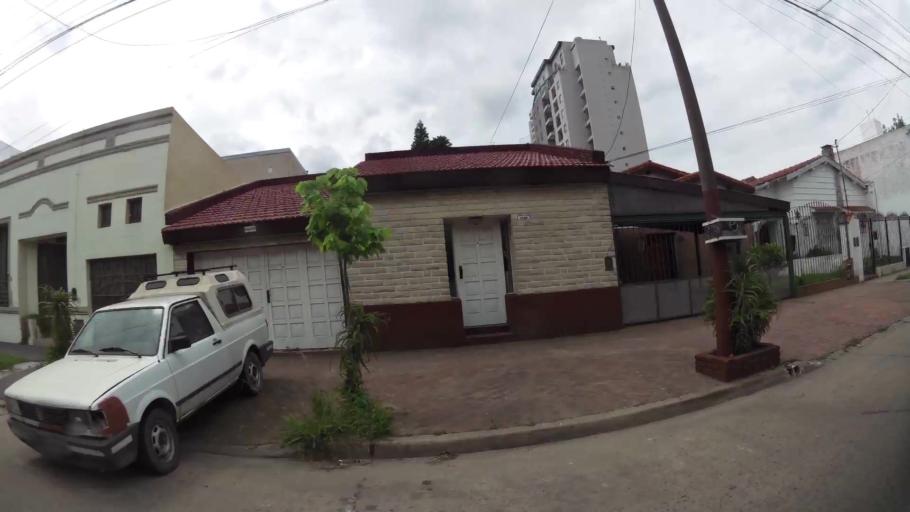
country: AR
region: Buenos Aires
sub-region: Partido de Campana
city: Campana
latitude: -34.1648
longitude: -58.9645
